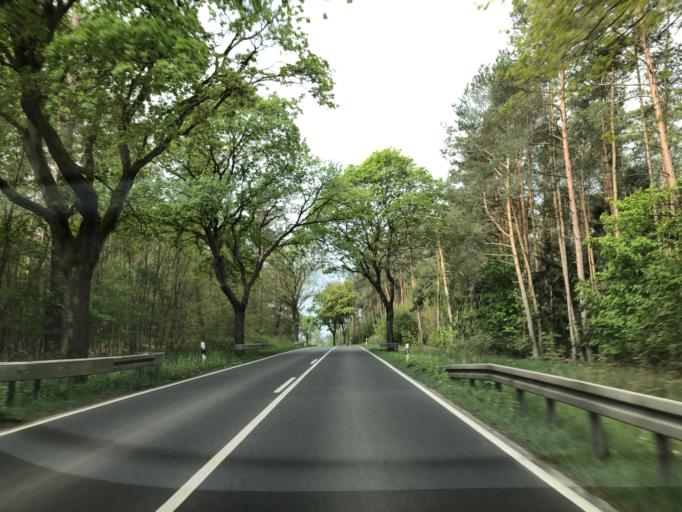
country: DE
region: Mecklenburg-Vorpommern
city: Dobbertin
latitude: 53.6855
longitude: 12.1068
